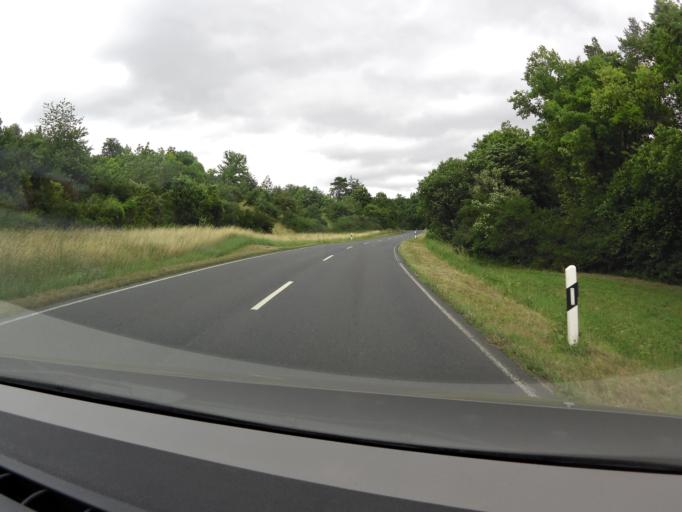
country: DE
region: Baden-Wuerttemberg
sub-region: Regierungsbezirk Stuttgart
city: Tauberbischofsheim
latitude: 49.6295
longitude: 9.6940
